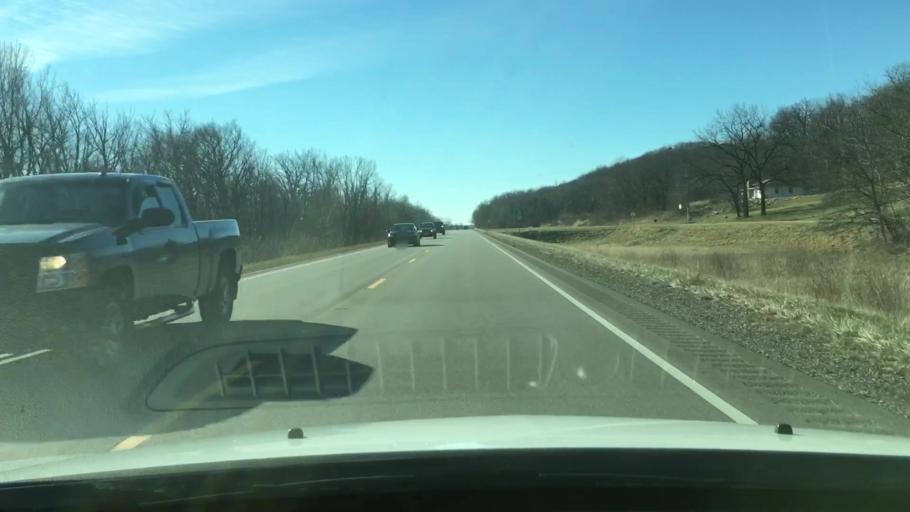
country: US
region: Illinois
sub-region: Peoria County
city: Glasford
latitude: 40.5329
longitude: -89.8716
